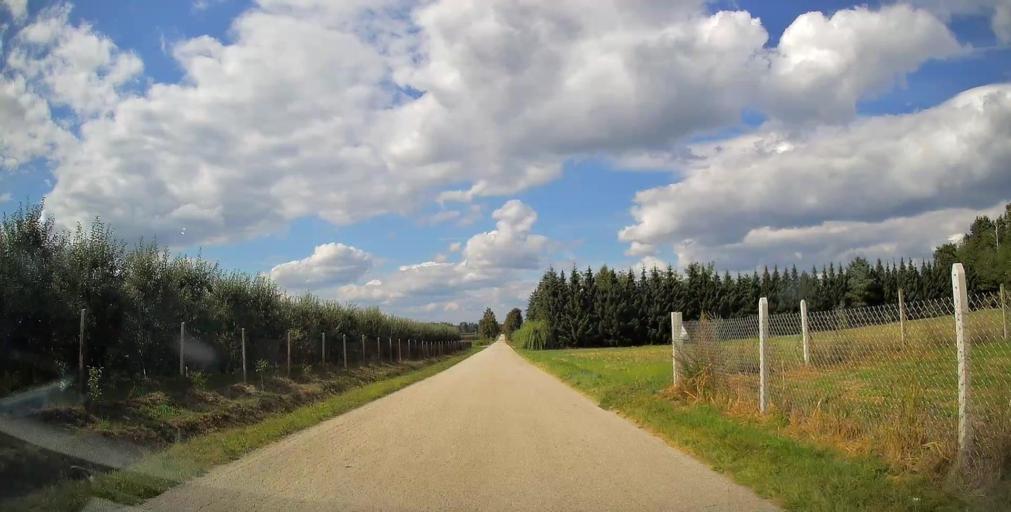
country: PL
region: Masovian Voivodeship
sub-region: Powiat grojecki
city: Goszczyn
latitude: 51.7046
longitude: 20.8959
